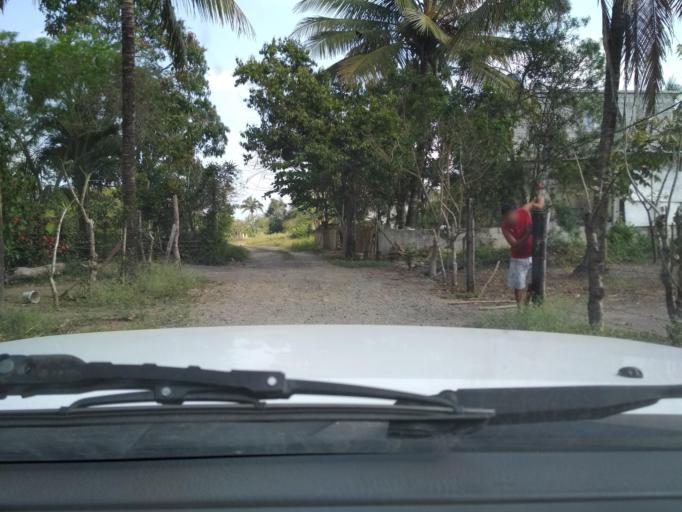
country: MX
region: Veracruz
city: El Tejar
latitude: 19.0834
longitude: -96.1655
